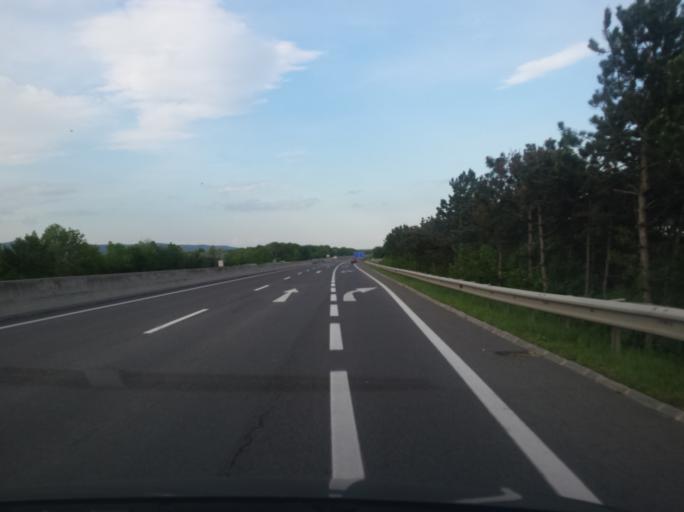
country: AT
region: Burgenland
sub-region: Eisenstadt-Umgebung
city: Wulkaprodersdorf
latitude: 47.8122
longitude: 16.4886
